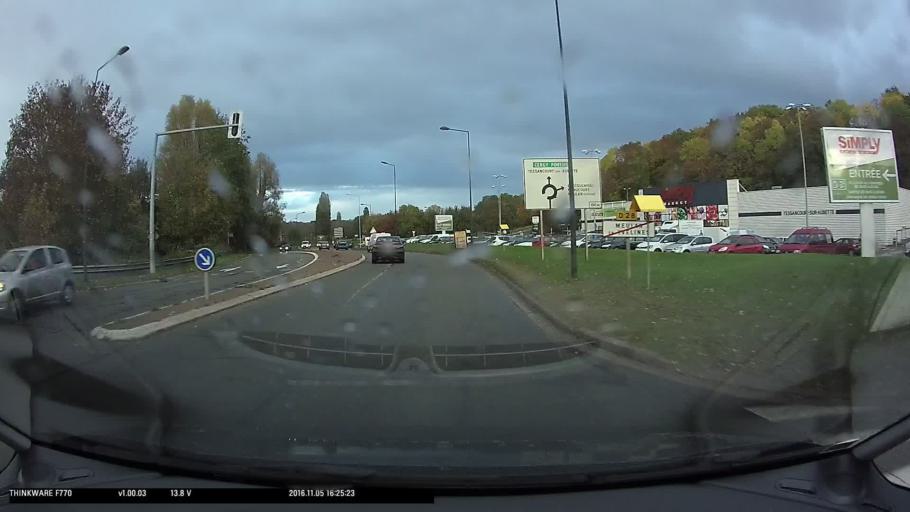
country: FR
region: Ile-de-France
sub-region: Departement des Yvelines
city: Meulan-en-Yvelines
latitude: 49.0119
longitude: 1.9073
